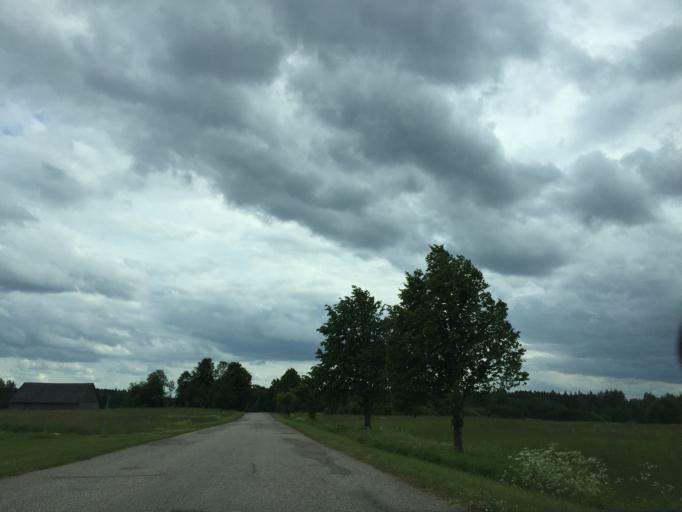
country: LV
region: Apes Novads
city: Ape
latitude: 57.4496
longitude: 26.3350
